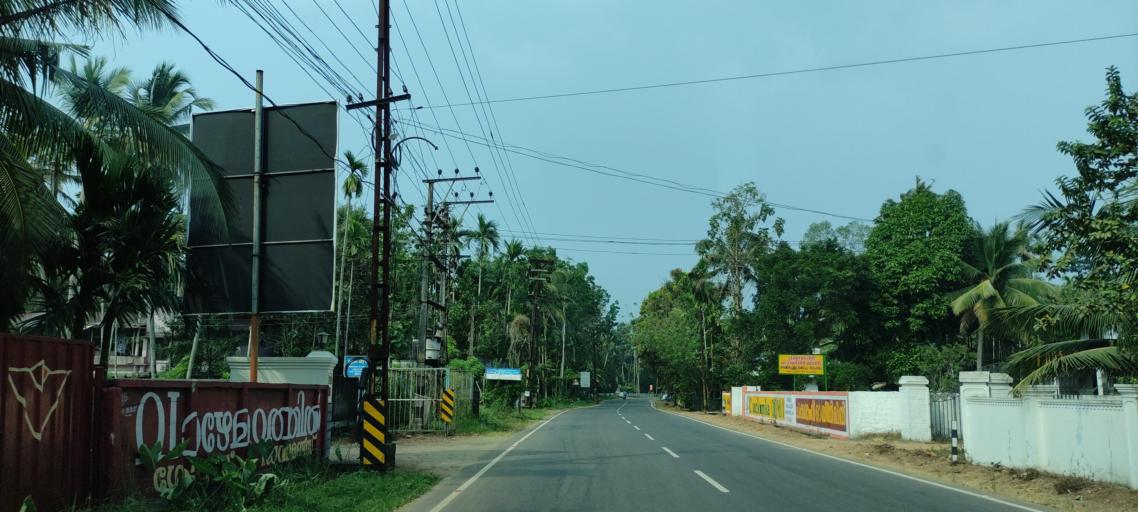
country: IN
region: Kerala
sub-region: Kottayam
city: Vaikam
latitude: 9.7632
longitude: 76.4147
